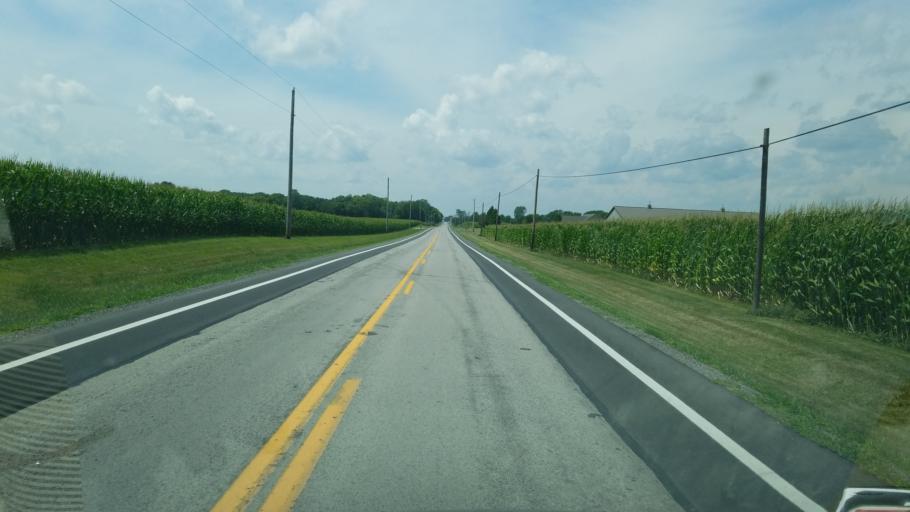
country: US
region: Ohio
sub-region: Hancock County
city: Arlington
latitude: 40.8923
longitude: -83.6722
